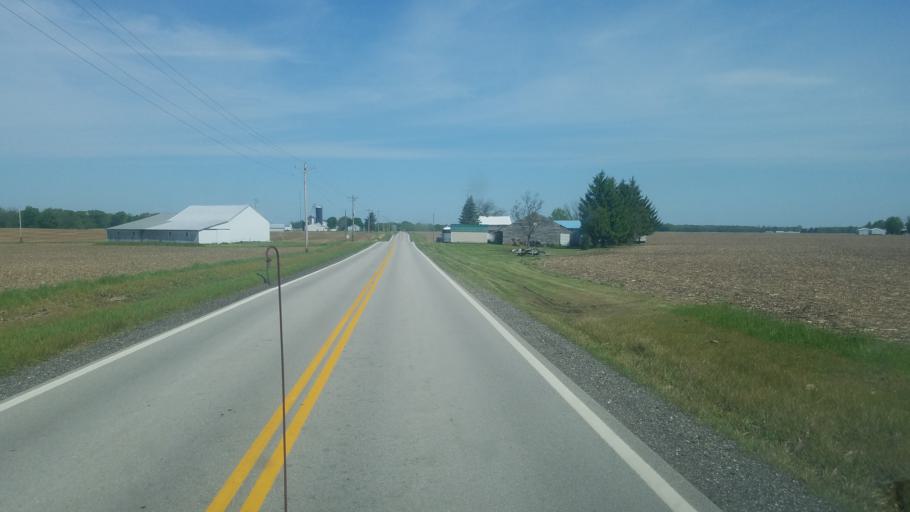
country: US
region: Ohio
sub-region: Crawford County
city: Bucyrus
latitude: 40.9374
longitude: -83.0571
